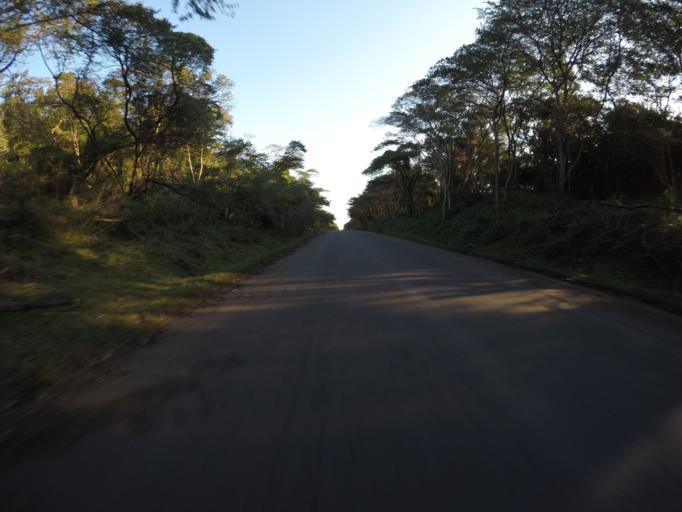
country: ZA
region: KwaZulu-Natal
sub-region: uThungulu District Municipality
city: KwaMbonambi
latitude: -28.6963
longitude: 32.2091
